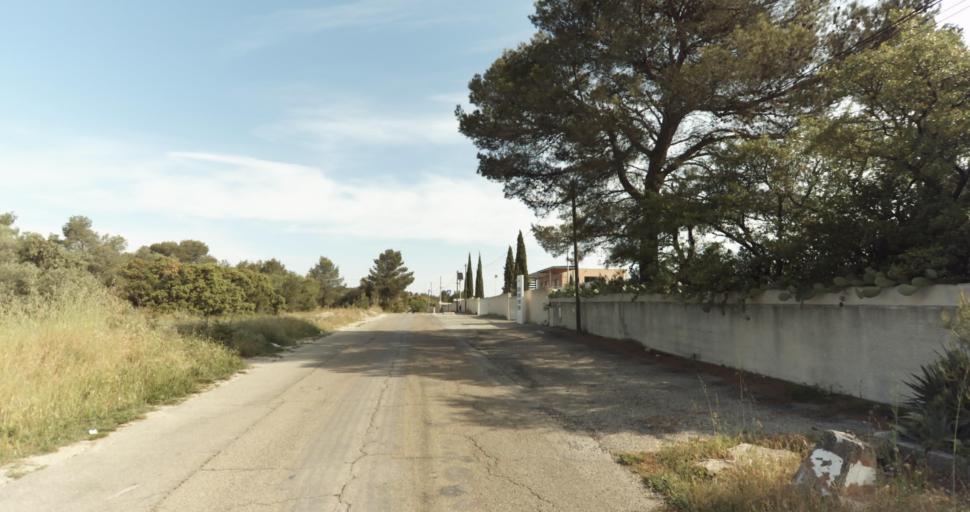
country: FR
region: Languedoc-Roussillon
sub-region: Departement du Gard
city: Nimes
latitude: 43.8697
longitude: 4.3795
